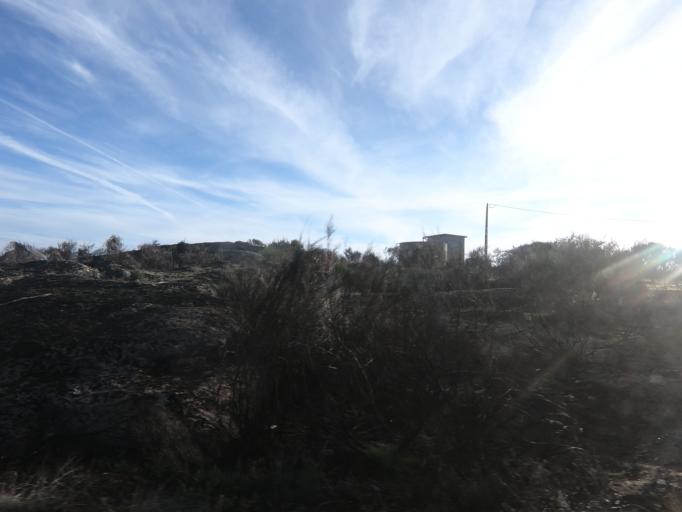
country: PT
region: Vila Real
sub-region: Sabrosa
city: Sabrosa
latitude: 41.2969
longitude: -7.6112
